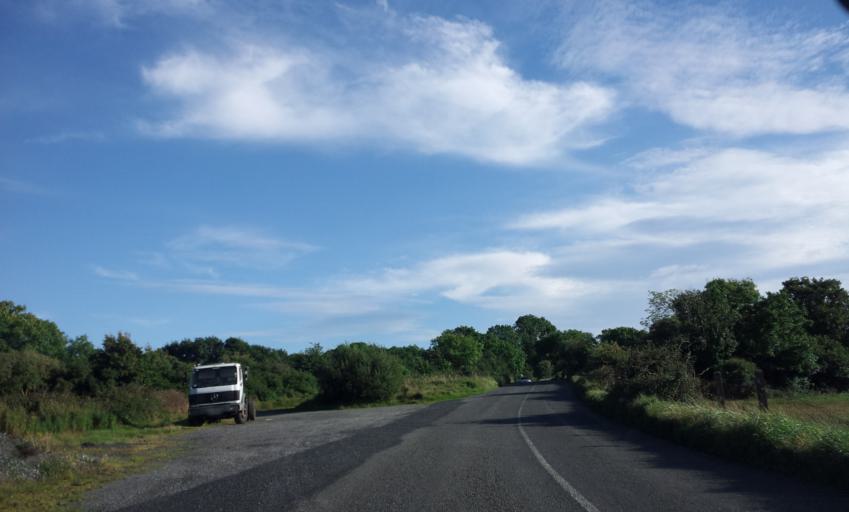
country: IE
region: Munster
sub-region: An Clar
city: Ennis
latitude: 52.9543
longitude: -9.0705
